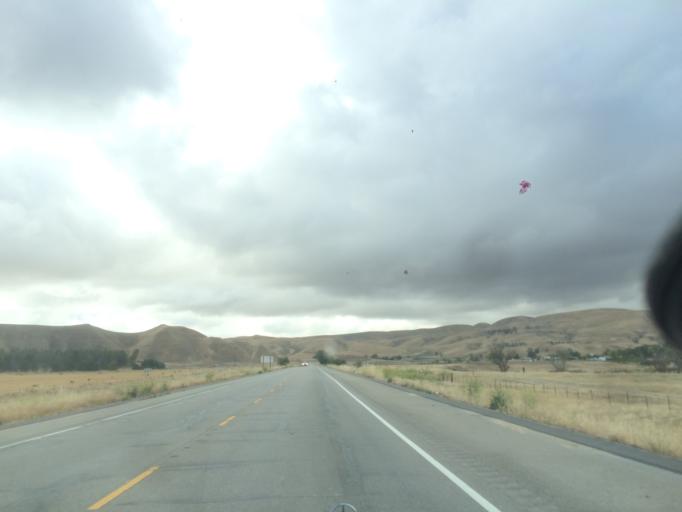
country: US
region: California
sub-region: San Luis Obispo County
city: Shandon
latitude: 35.6624
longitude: -120.3759
